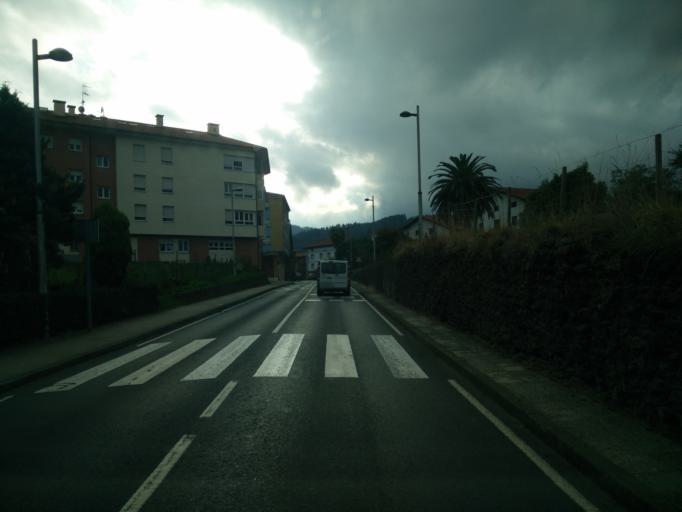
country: ES
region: Basque Country
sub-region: Bizkaia
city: Berriatua
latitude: 43.3100
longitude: -2.4666
